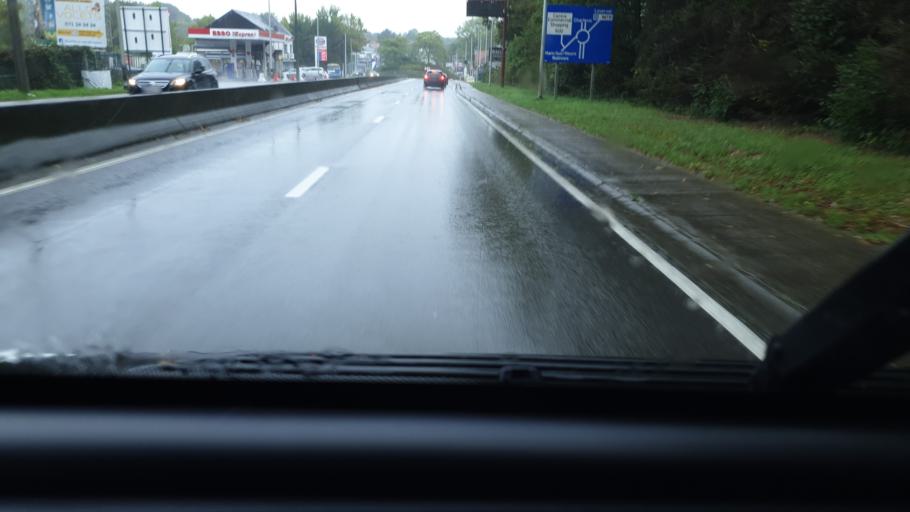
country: BE
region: Wallonia
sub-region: Province du Hainaut
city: Charleroi
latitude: 50.3596
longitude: 4.4702
